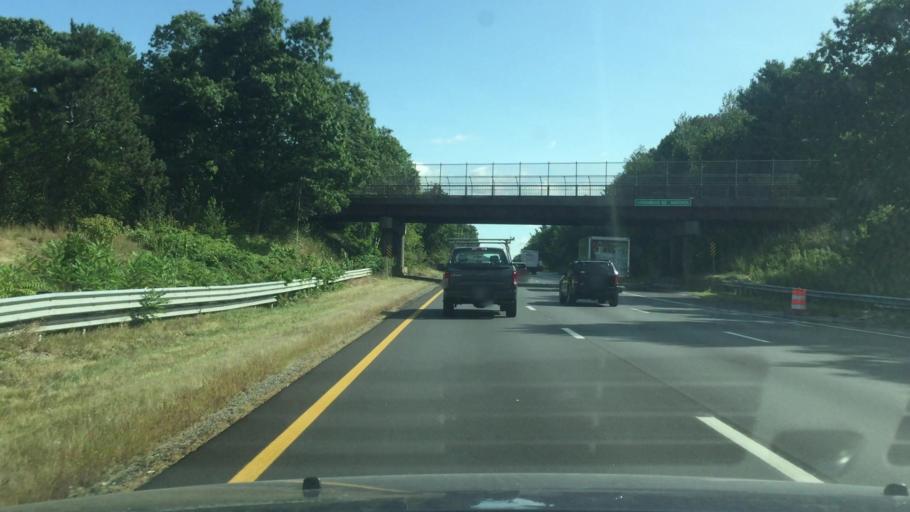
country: US
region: Massachusetts
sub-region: Essex County
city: Lawrence
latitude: 42.6668
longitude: -71.1901
